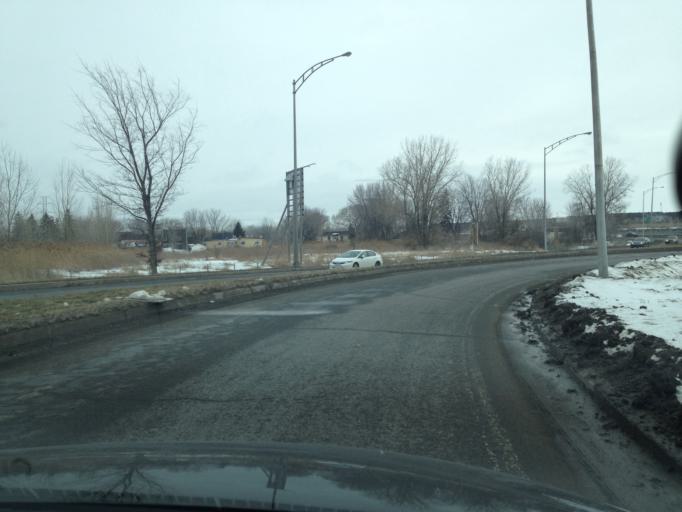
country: CA
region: Quebec
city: Dollard-Des Ormeaux
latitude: 45.5244
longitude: -73.7748
